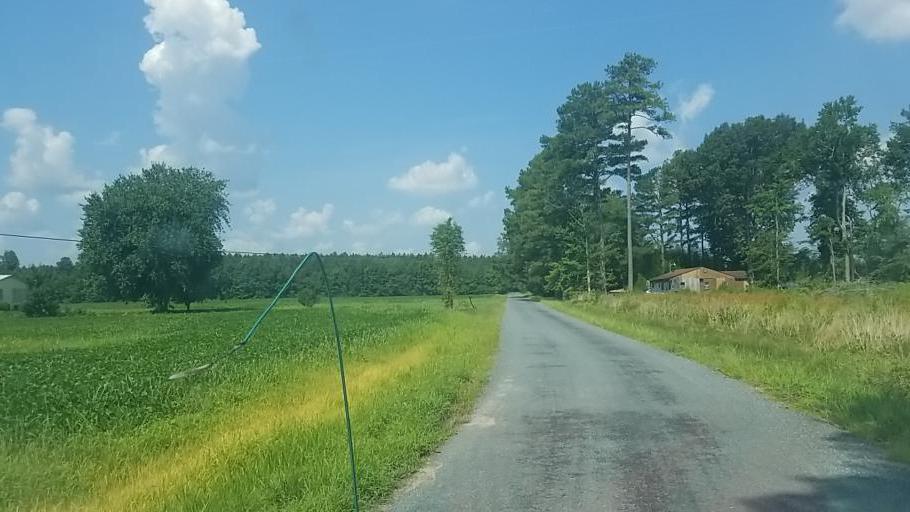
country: US
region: Maryland
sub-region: Worcester County
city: Berlin
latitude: 38.2850
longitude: -75.3037
